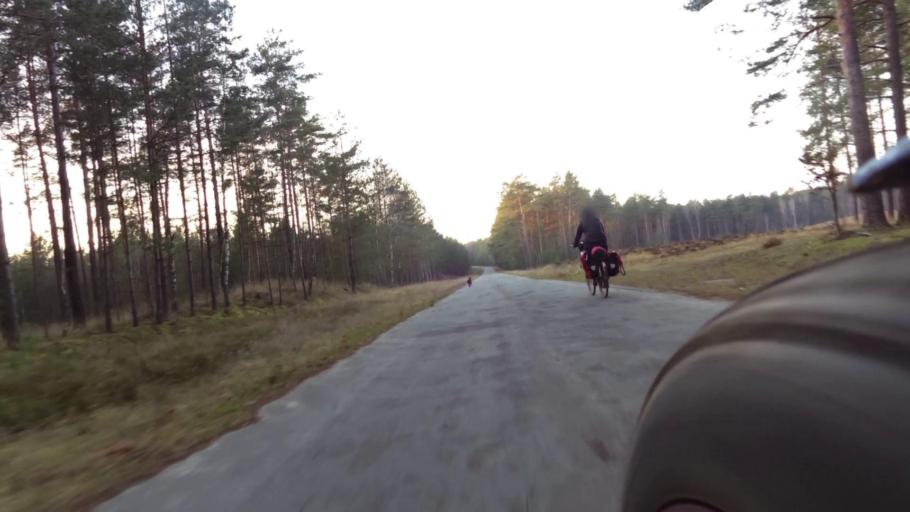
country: PL
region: West Pomeranian Voivodeship
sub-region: Powiat szczecinecki
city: Borne Sulinowo
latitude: 53.5671
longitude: 16.5922
